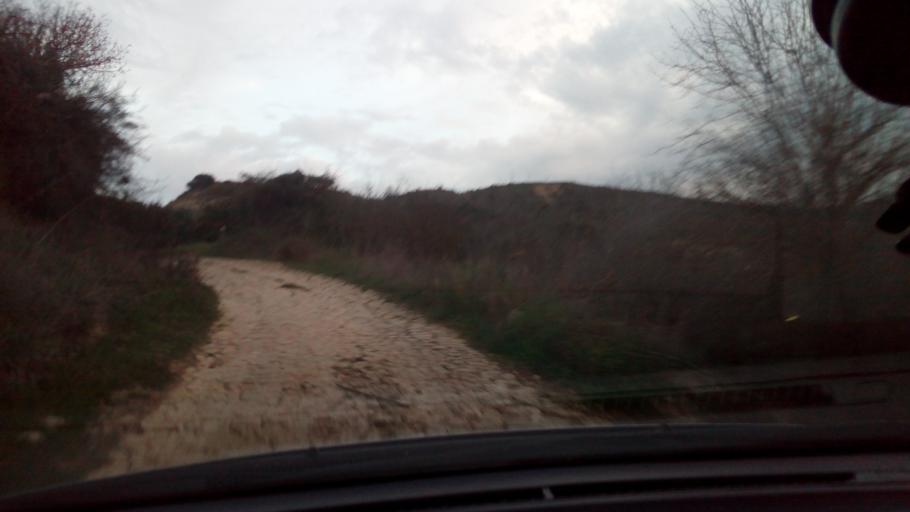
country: CY
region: Pafos
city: Polis
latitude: 34.9518
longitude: 32.4683
